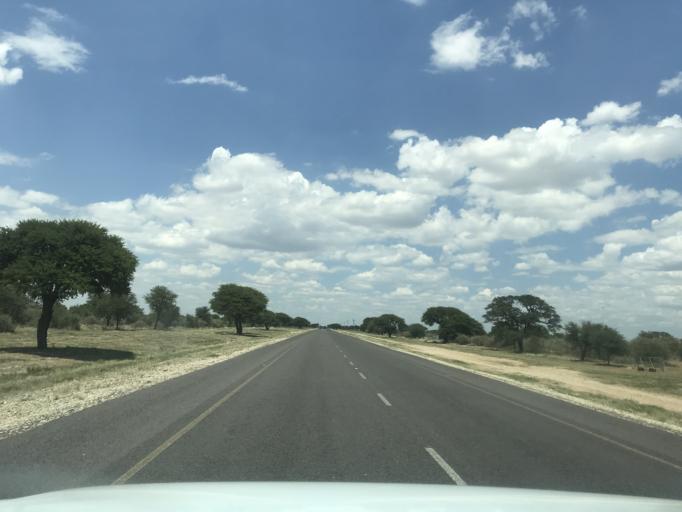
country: BW
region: South East
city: Janeng
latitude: -25.6326
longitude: 25.1541
